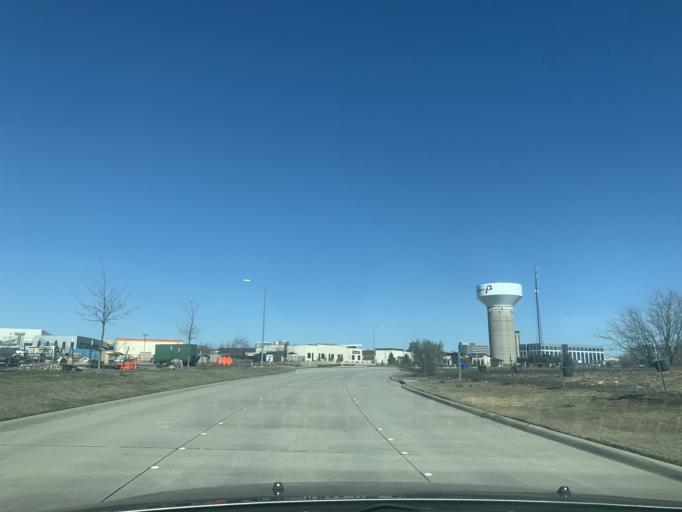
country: US
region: Texas
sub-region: Denton County
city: The Colony
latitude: 33.0668
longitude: -96.8326
